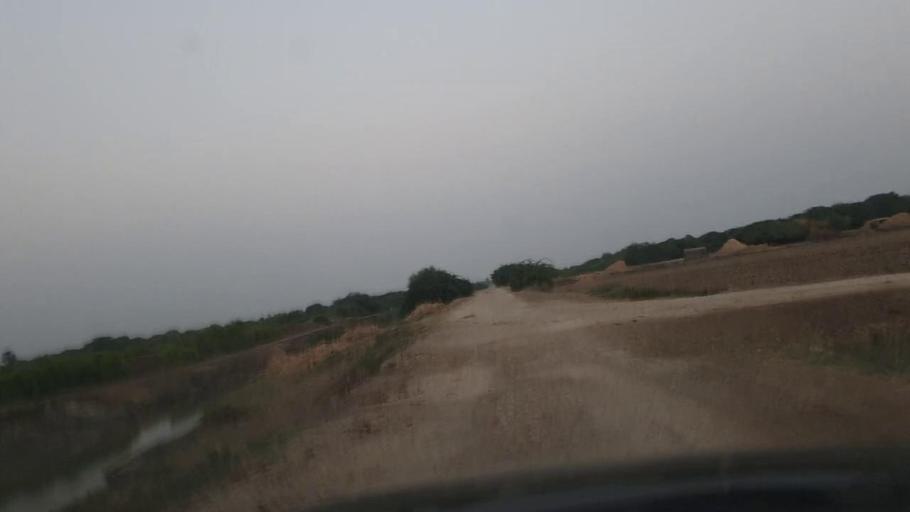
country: PK
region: Sindh
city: Mirpur Sakro
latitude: 24.6364
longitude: 67.7302
